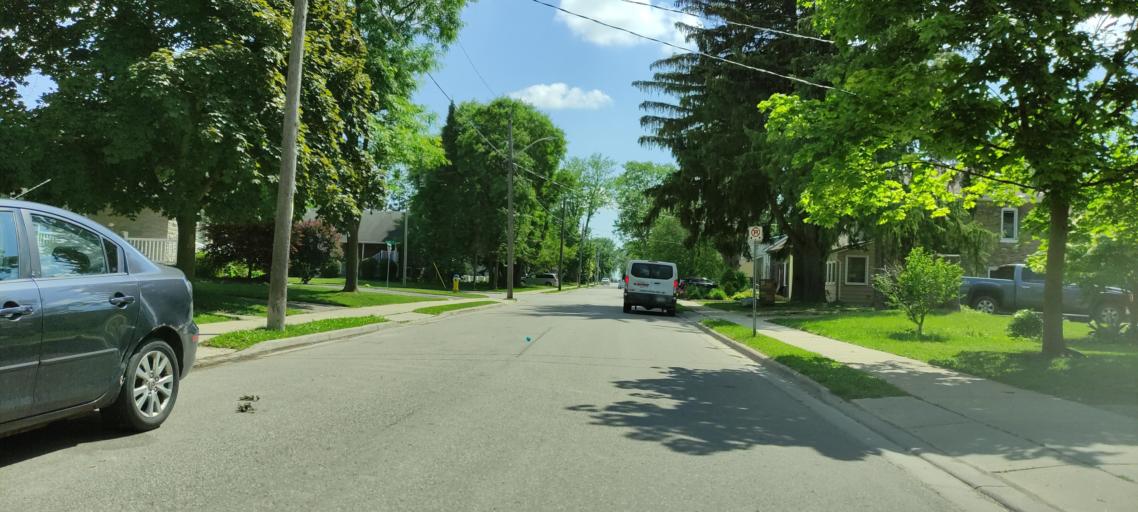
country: CA
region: Ontario
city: Stratford
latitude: 43.3611
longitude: -80.9885
